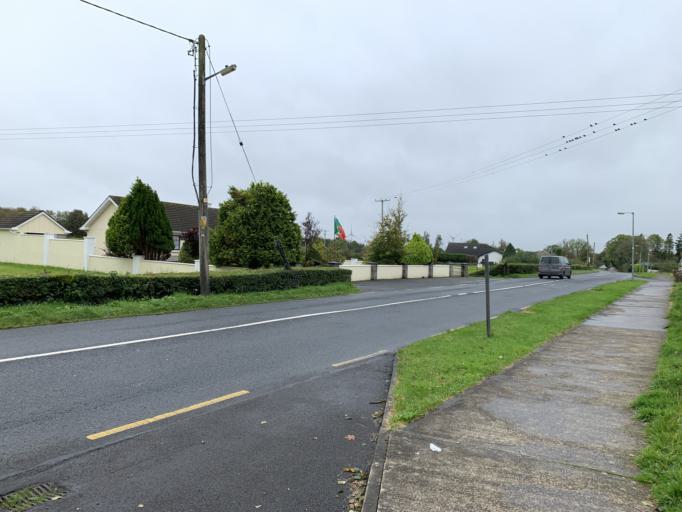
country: IE
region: Connaught
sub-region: Roscommon
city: Ballaghaderreen
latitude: 53.8977
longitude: -8.5843
